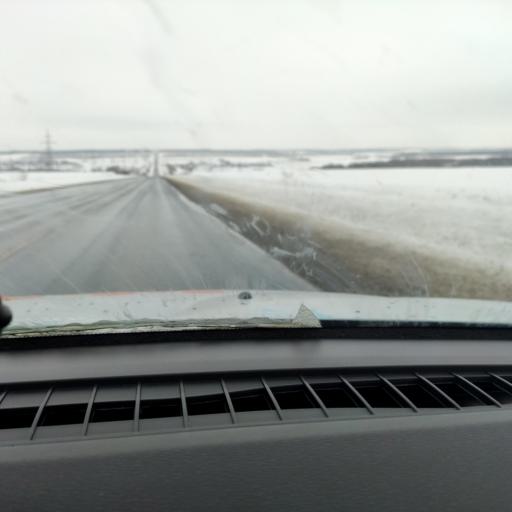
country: RU
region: Samara
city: Novokuybyshevsk
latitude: 53.0100
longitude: 50.0426
